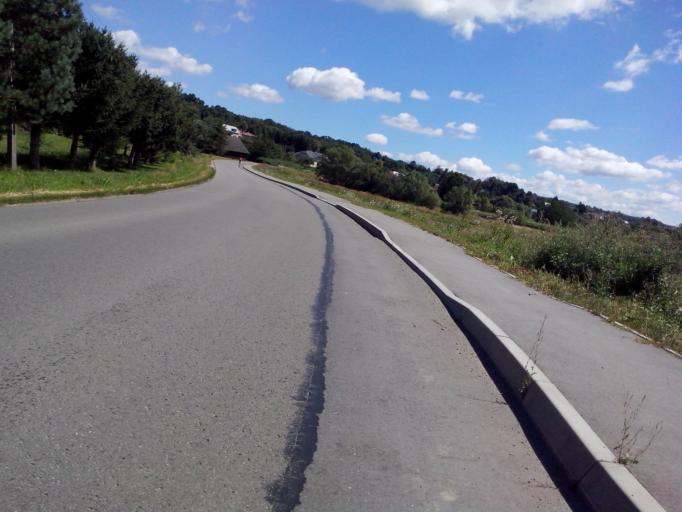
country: PL
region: Subcarpathian Voivodeship
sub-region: Powiat brzozowski
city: Domaradz
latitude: 49.7916
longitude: 21.9559
